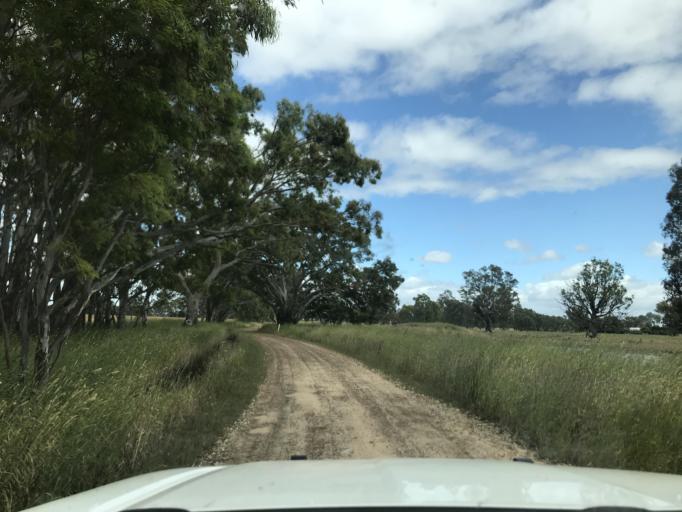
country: AU
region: South Australia
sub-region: Naracoorte and Lucindale
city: Naracoorte
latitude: -36.9000
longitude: 141.3973
